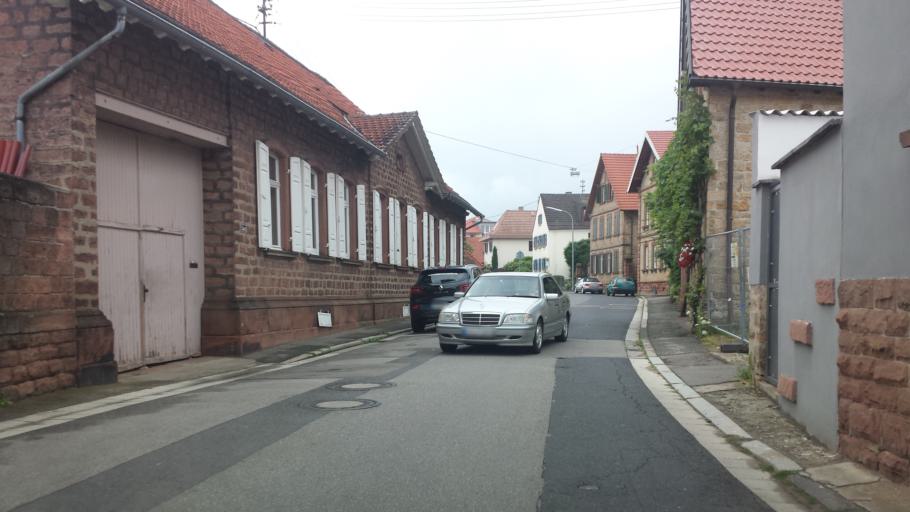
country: DE
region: Rheinland-Pfalz
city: Maikammer
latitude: 49.3193
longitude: 8.1359
